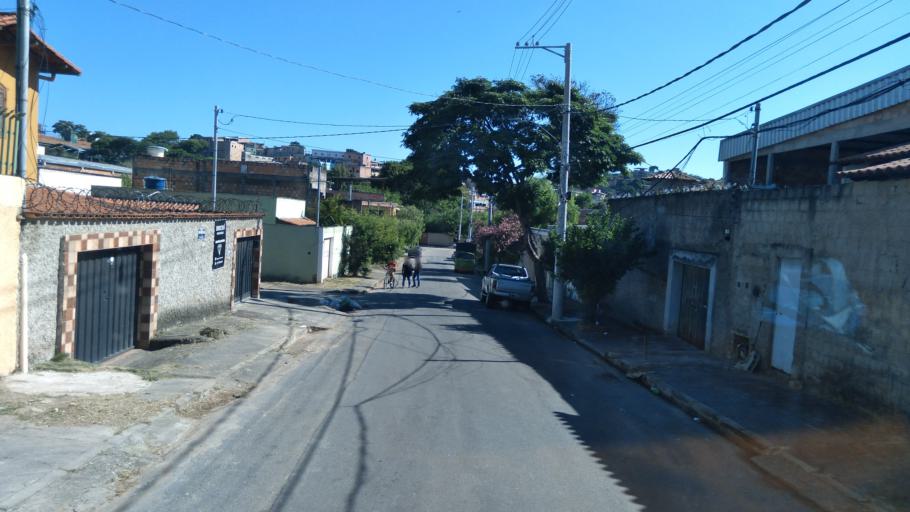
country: BR
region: Minas Gerais
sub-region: Belo Horizonte
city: Belo Horizonte
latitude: -19.8442
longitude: -43.9078
